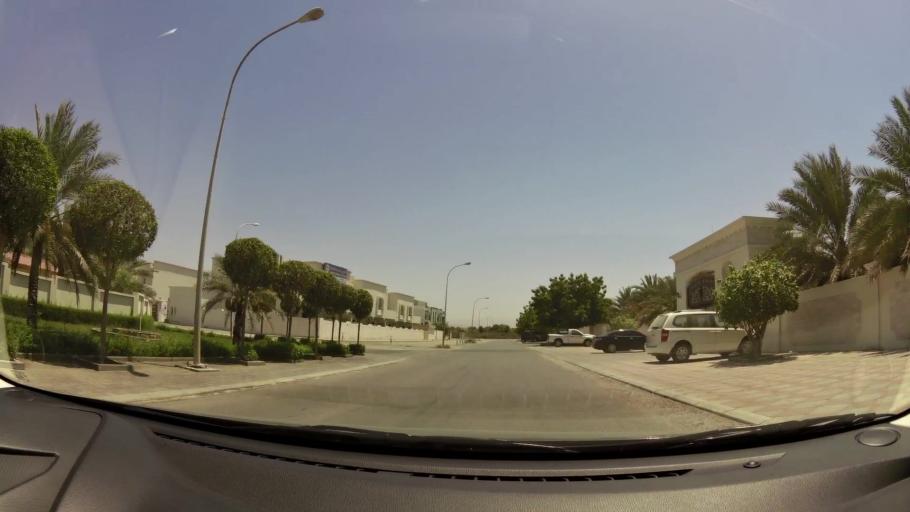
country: OM
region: Muhafazat Masqat
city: As Sib al Jadidah
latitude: 23.6164
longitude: 58.2356
